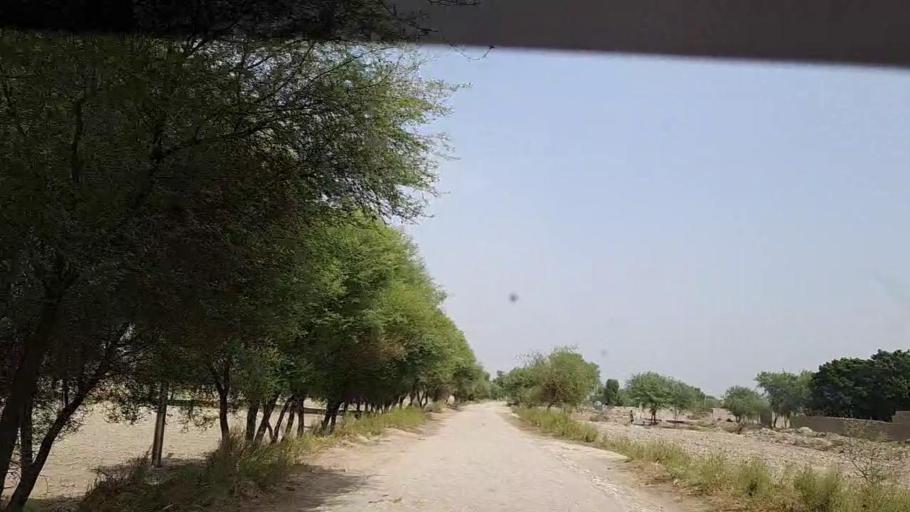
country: PK
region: Sindh
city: Khairpur Nathan Shah
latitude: 27.0805
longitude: 67.6787
